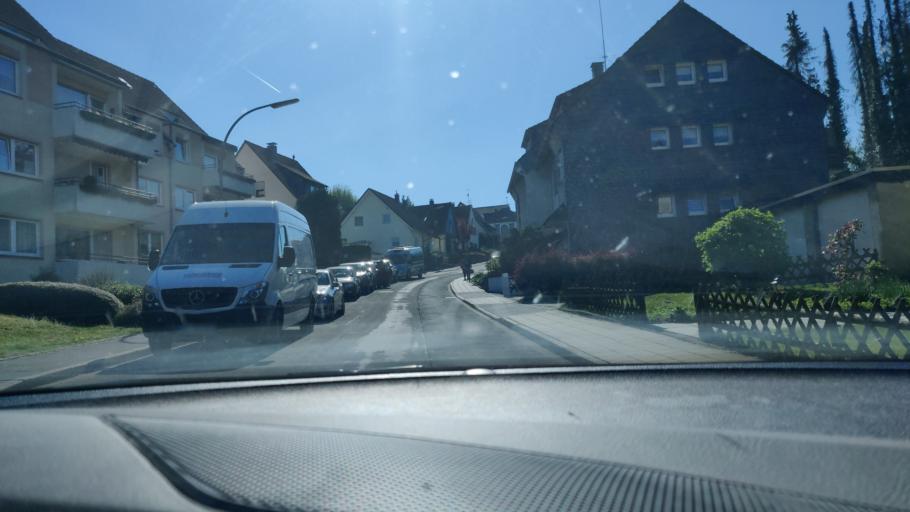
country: DE
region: North Rhine-Westphalia
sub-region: Regierungsbezirk Dusseldorf
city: Velbert
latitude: 51.3475
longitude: 7.0362
